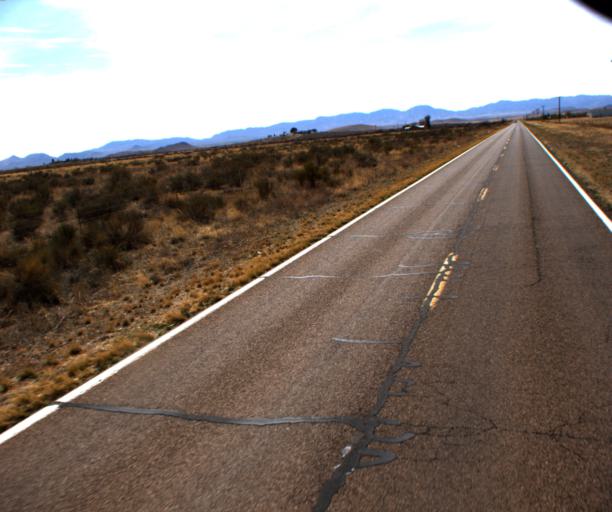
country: US
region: Arizona
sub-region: Cochise County
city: Willcox
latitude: 31.8837
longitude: -109.6726
